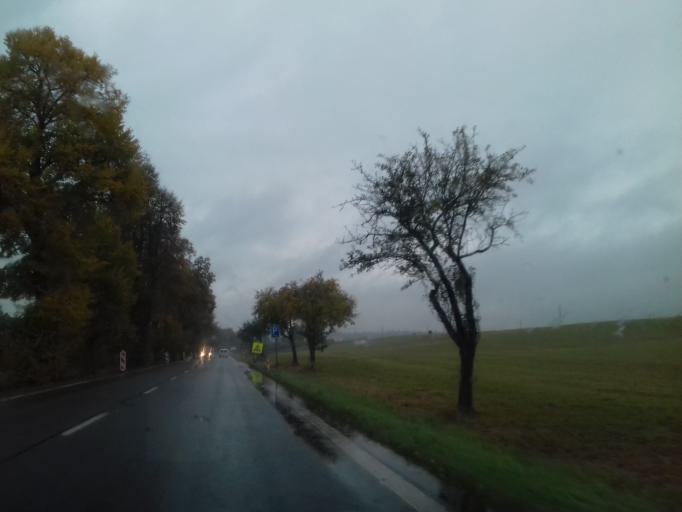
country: CZ
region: Liberecky
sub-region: Okres Semily
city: Turnov
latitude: 50.5638
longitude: 15.1928
